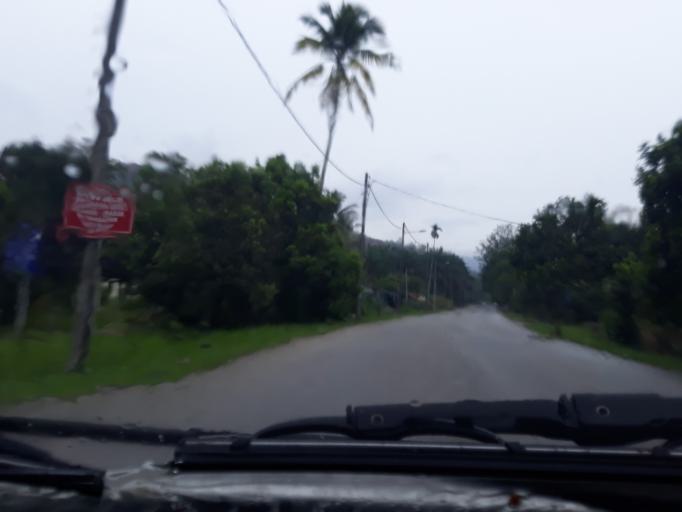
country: MY
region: Kedah
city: Kulim
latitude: 5.2714
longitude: 100.6143
